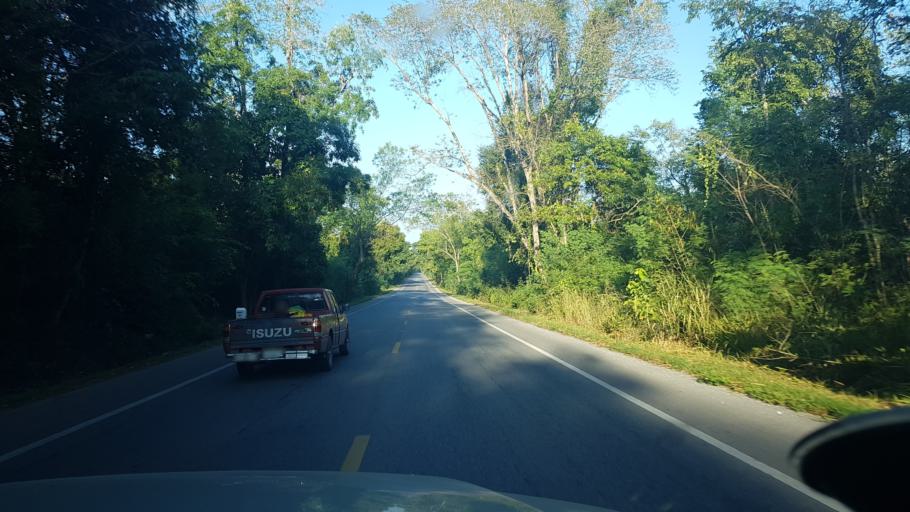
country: TH
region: Khon Kaen
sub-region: Amphoe Phu Pha Man
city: Phu Pha Man
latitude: 16.6279
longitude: 101.8458
